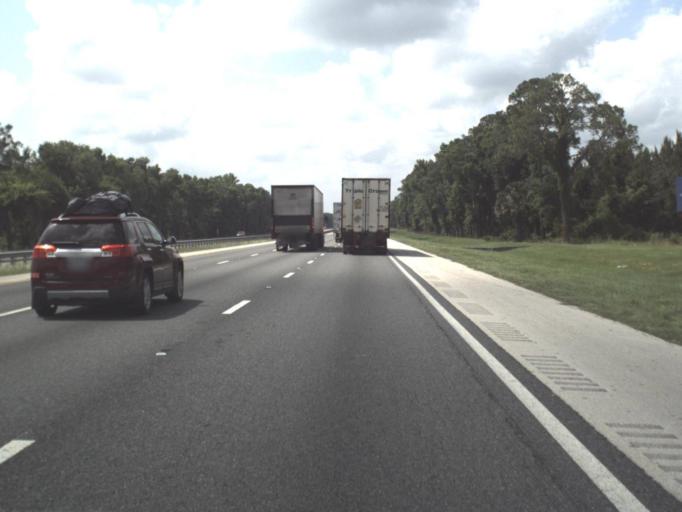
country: US
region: Florida
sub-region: Saint Johns County
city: Saint Augustine
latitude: 29.9326
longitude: -81.4225
